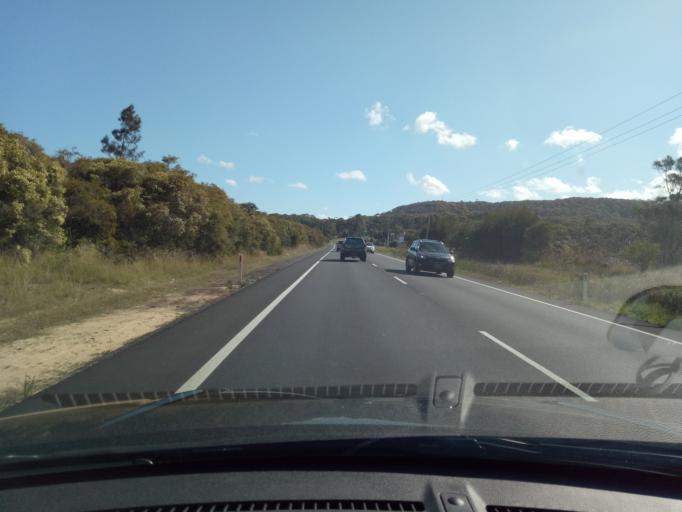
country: AU
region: New South Wales
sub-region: Gosford Shire
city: Forresters Beach
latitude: -33.4119
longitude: 151.4564
